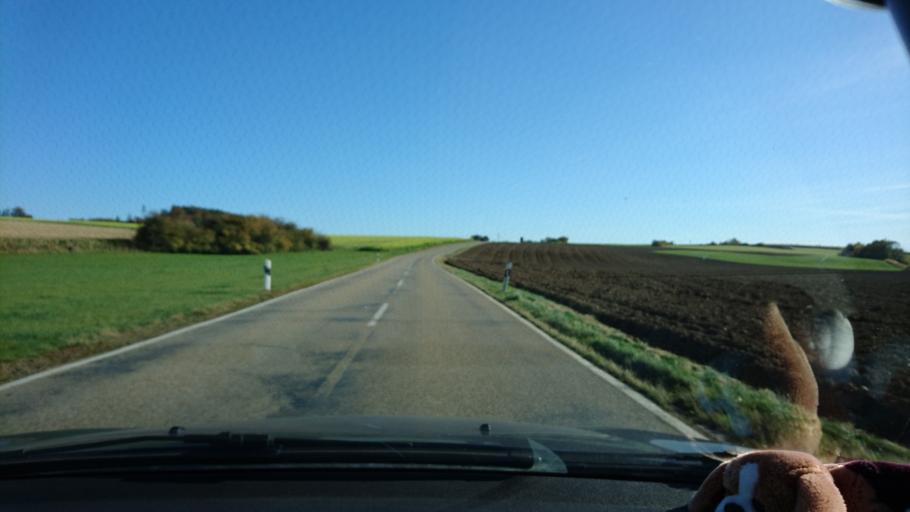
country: DE
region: Bavaria
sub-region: Upper Bavaria
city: Anzing
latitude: 48.1380
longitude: 11.8273
